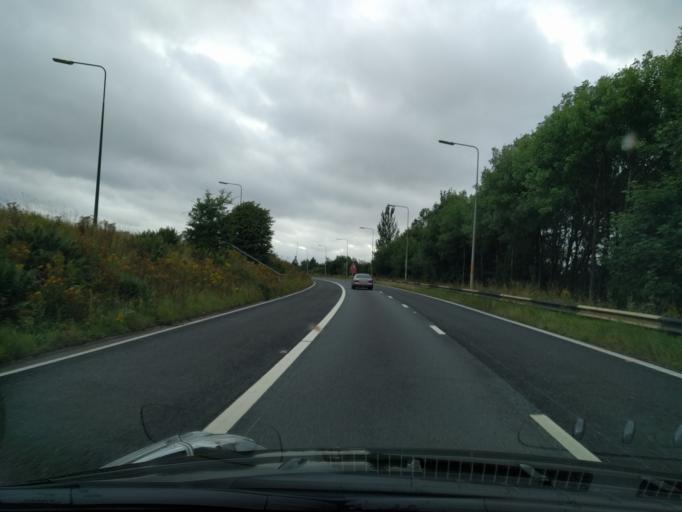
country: GB
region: England
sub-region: Warrington
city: Croft
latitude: 53.4296
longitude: -2.5564
